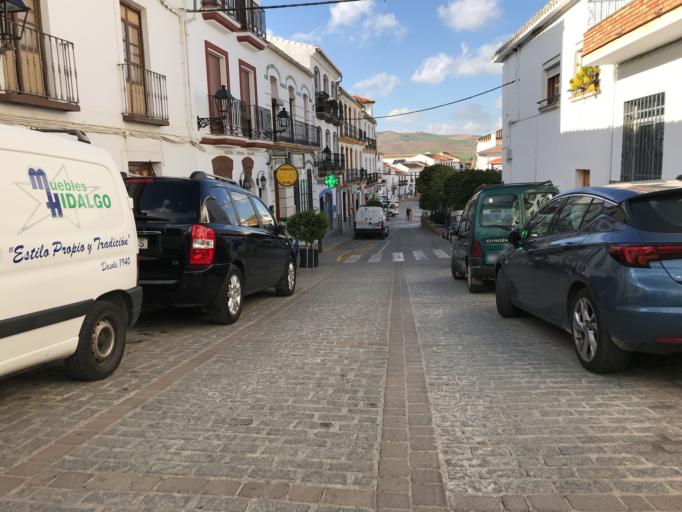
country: ES
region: Andalusia
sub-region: Provincia de Malaga
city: Ardales
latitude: 36.8778
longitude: -4.8465
